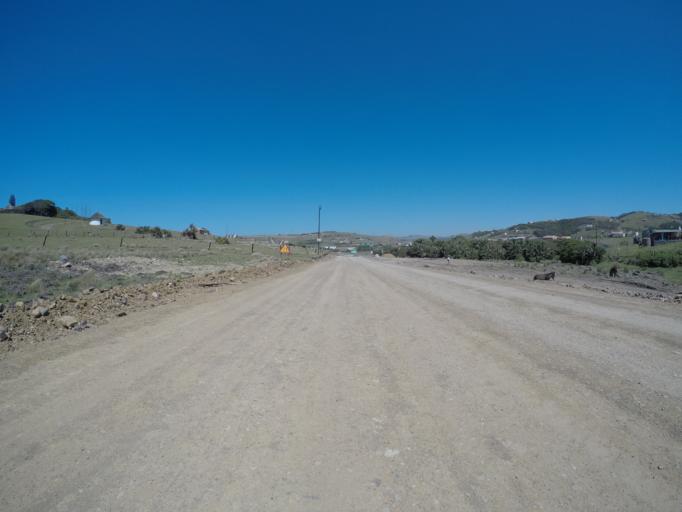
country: ZA
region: Eastern Cape
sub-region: OR Tambo District Municipality
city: Libode
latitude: -32.0289
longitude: 29.1136
